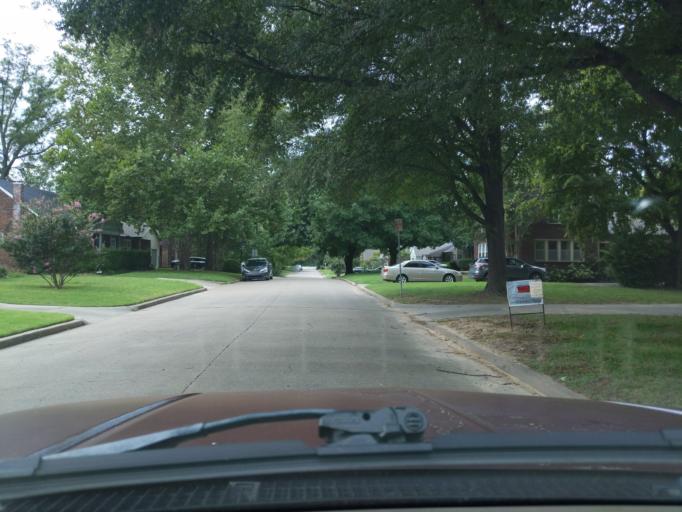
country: US
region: Oklahoma
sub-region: Tulsa County
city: Tulsa
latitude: 36.1107
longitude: -95.9808
